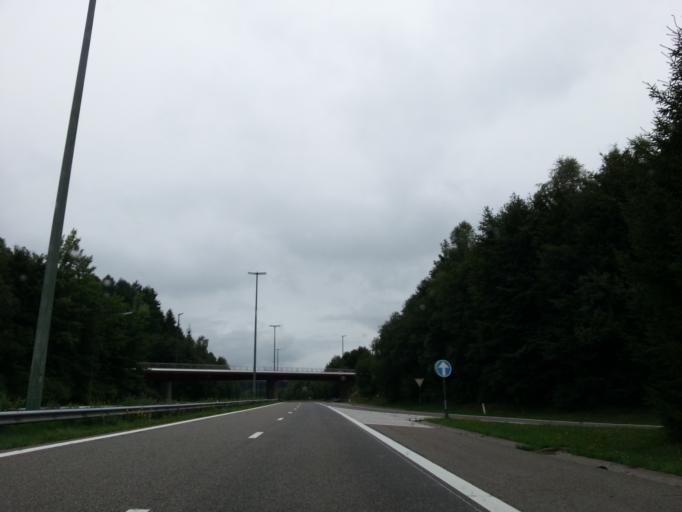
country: BE
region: Wallonia
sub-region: Province de Liege
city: Saint-Vith
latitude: 50.2538
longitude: 6.1694
